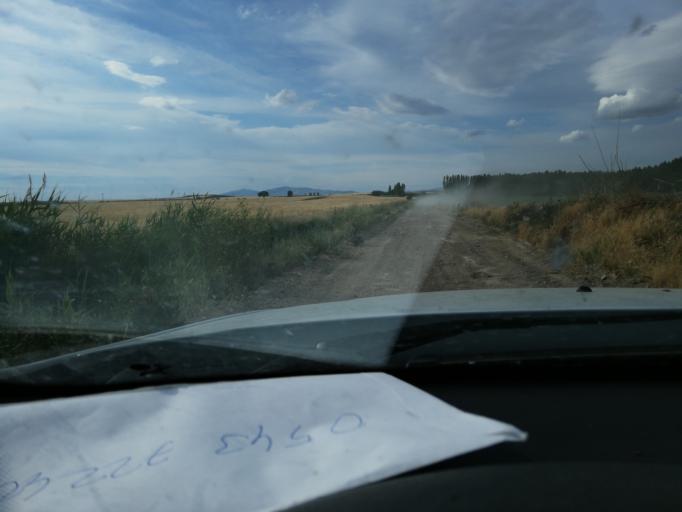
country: TR
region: Kirsehir
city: Kirsehir
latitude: 38.9992
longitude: 34.1246
